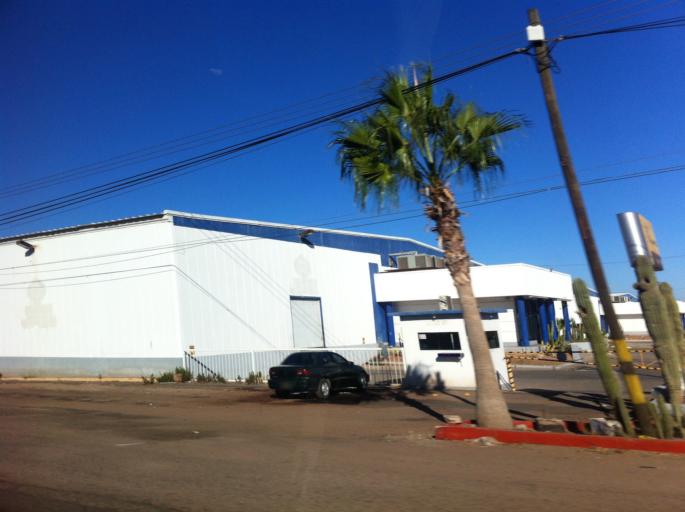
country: MX
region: Sonora
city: Heroica Guaymas
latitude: 27.9602
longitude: -110.9355
